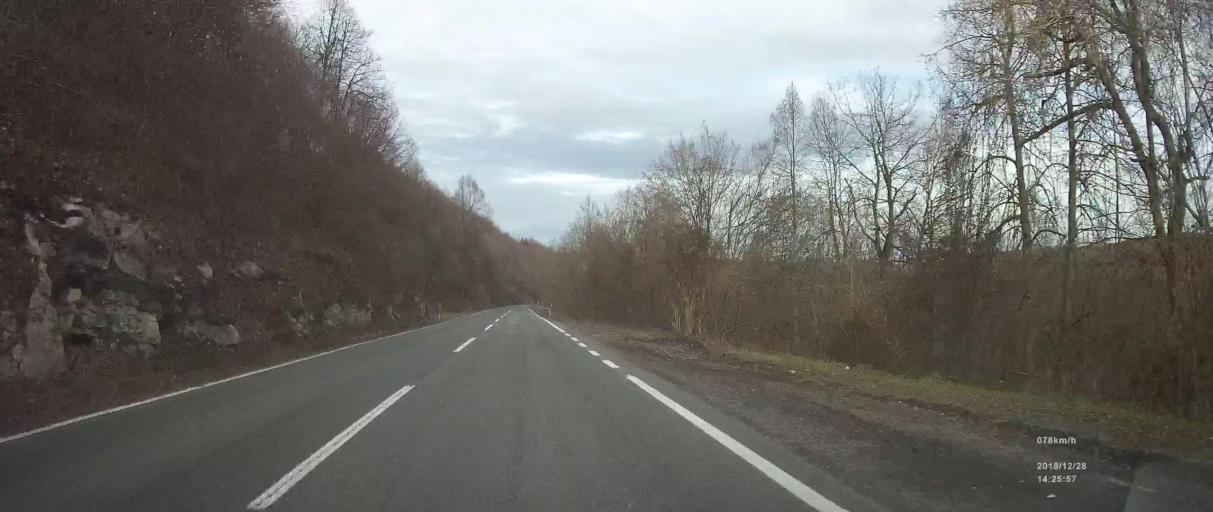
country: HR
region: Primorsko-Goranska
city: Vrbovsko
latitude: 45.3996
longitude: 15.1078
